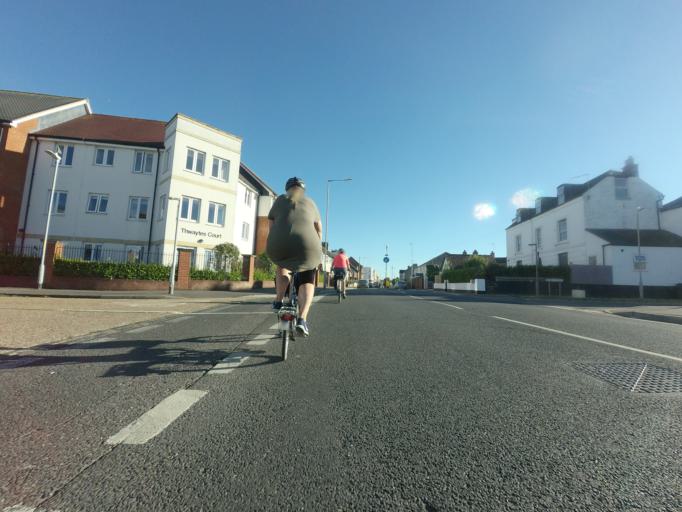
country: GB
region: England
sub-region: Kent
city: Herne Bay
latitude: 51.3697
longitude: 1.1142
